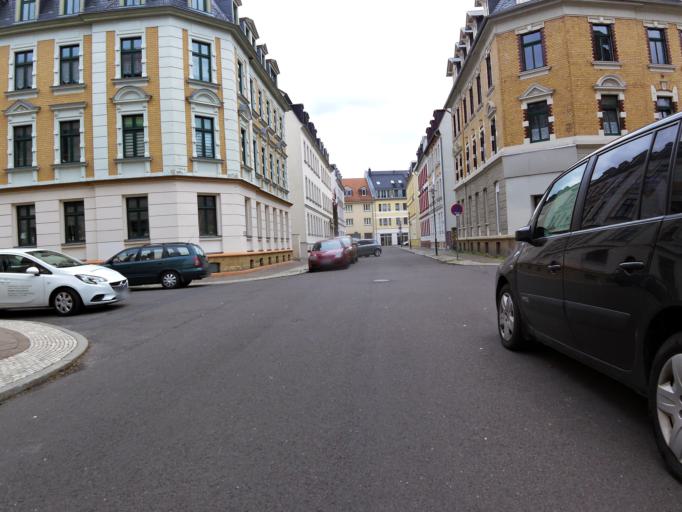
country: DE
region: Saxony
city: Markkleeberg
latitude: 51.2810
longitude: 12.3752
